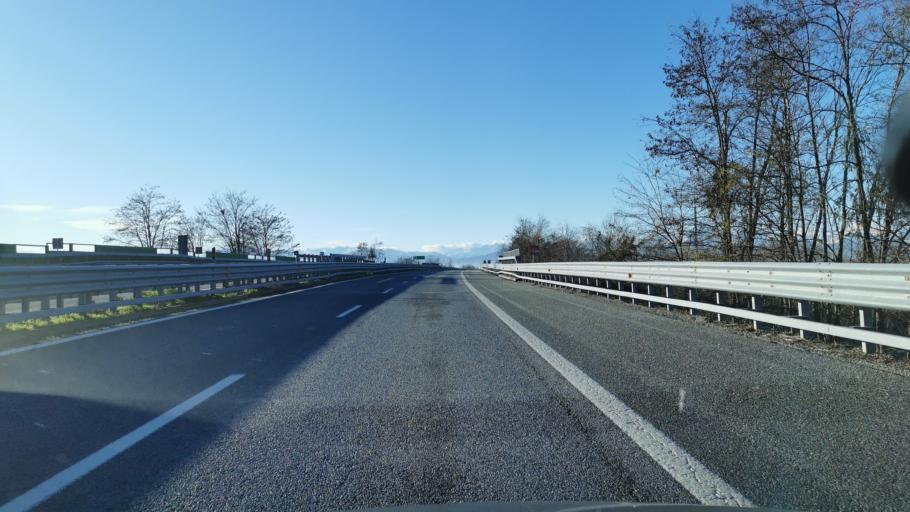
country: IT
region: Piedmont
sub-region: Provincia di Cuneo
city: Trinita
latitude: 44.4682
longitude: 7.7699
